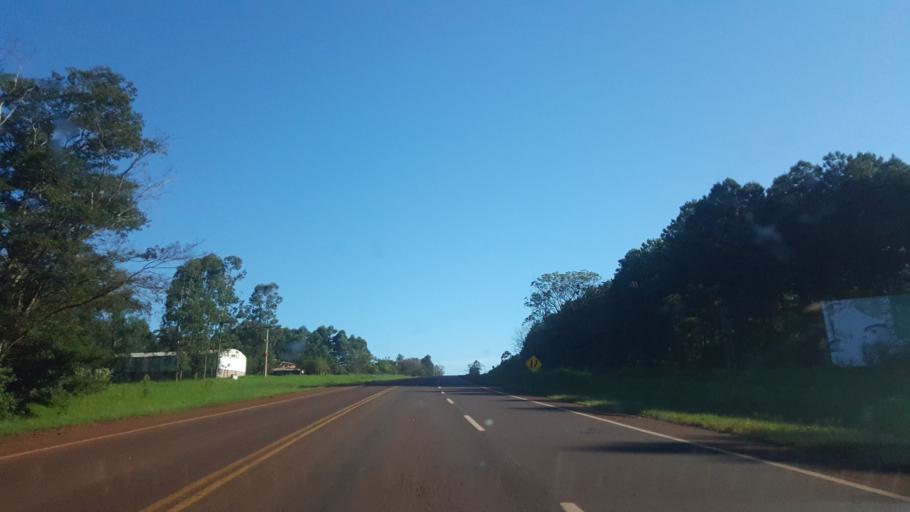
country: AR
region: Misiones
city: Puerto Esperanza
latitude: -26.1679
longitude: -54.5845
